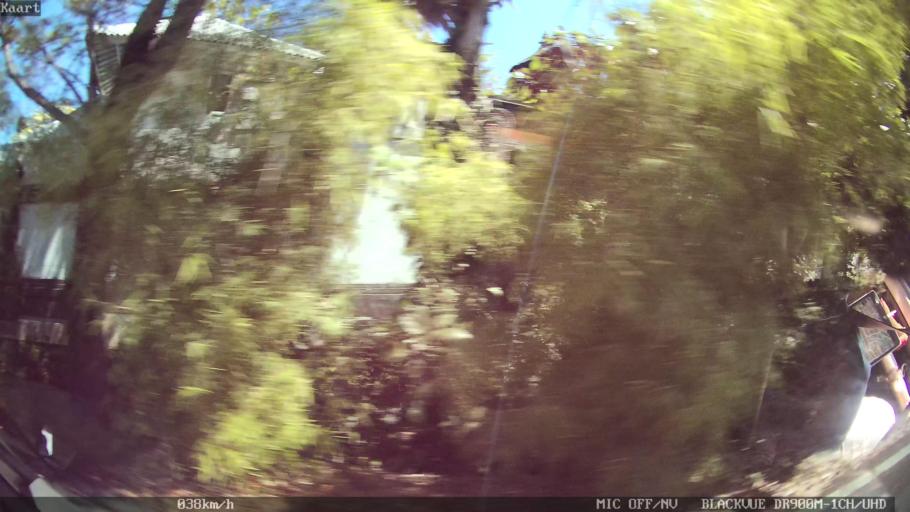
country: ID
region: Bali
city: Denpasar
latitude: -8.6707
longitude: 115.1688
